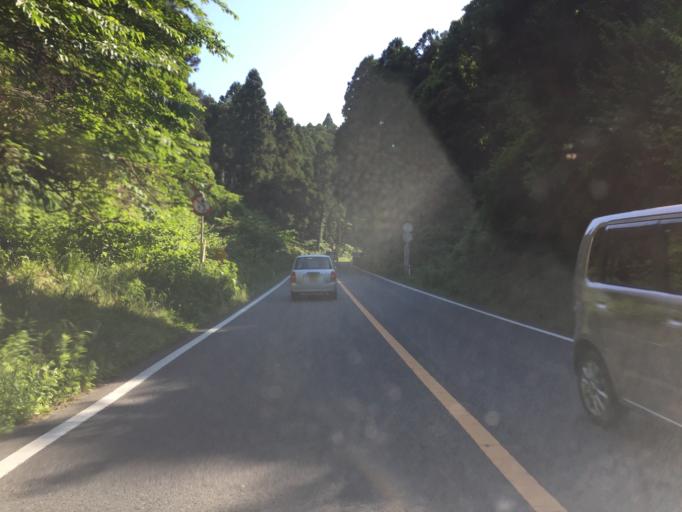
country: JP
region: Fukushima
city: Iwaki
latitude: 36.9494
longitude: 140.8258
